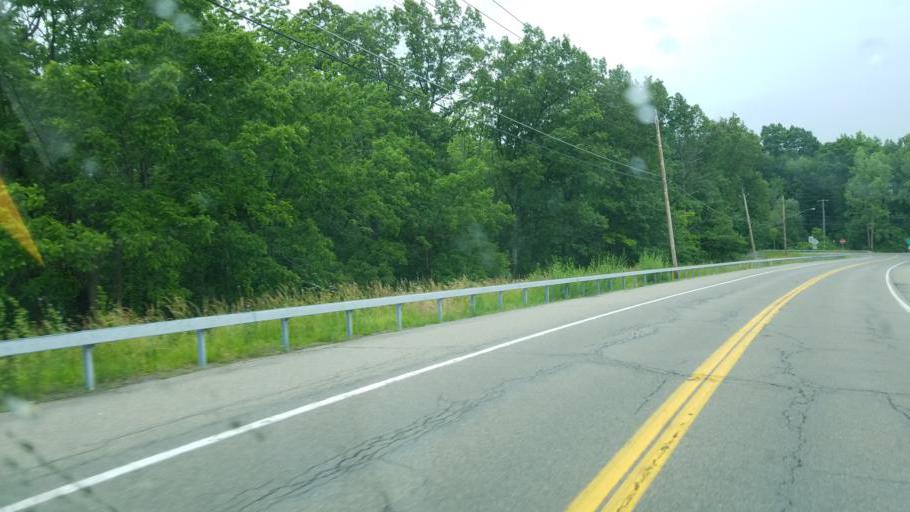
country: US
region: New York
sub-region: Niagara County
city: Youngstown
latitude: 43.2694
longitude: -79.0057
